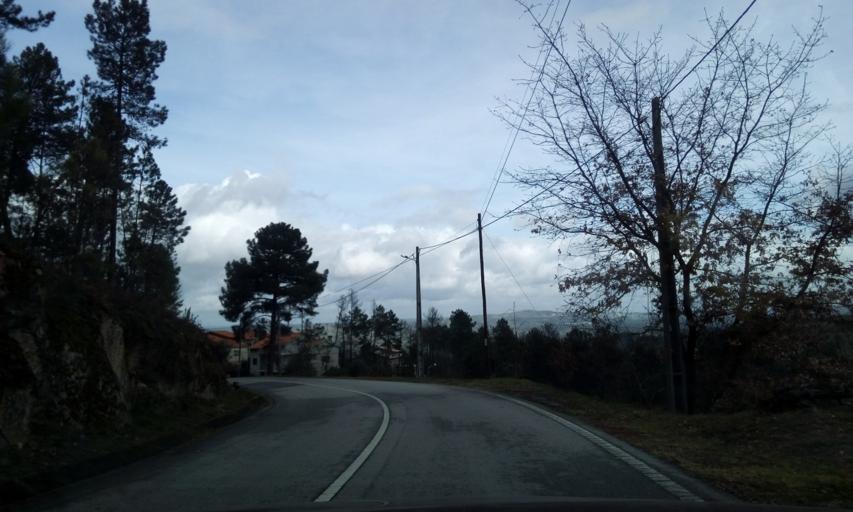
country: PT
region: Guarda
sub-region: Fornos de Algodres
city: Fornos de Algodres
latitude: 40.6648
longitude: -7.6103
